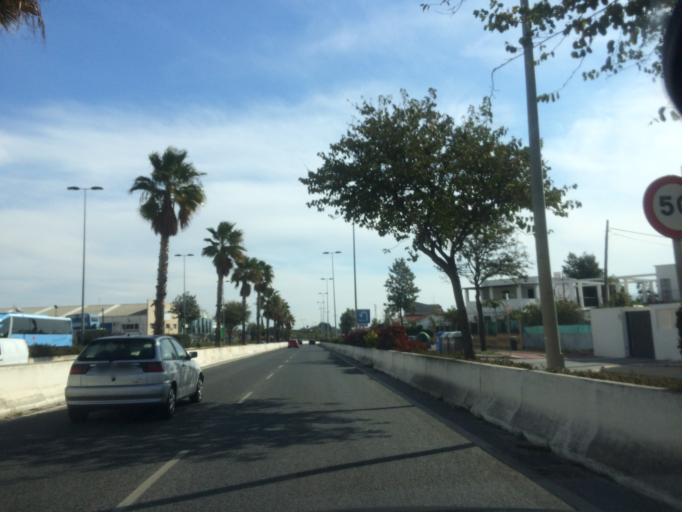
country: ES
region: Andalusia
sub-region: Provincia de Malaga
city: Torremolinos
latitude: 36.6597
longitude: -4.4954
